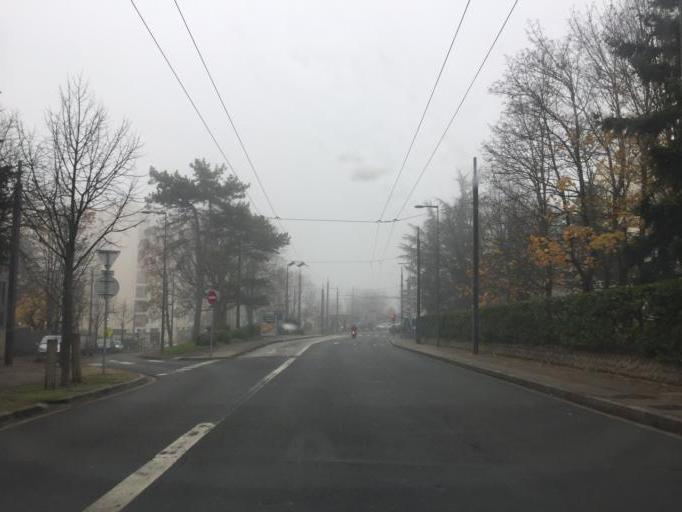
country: FR
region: Rhone-Alpes
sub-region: Departement du Rhone
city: Caluire-et-Cuire
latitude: 45.7861
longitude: 4.8376
